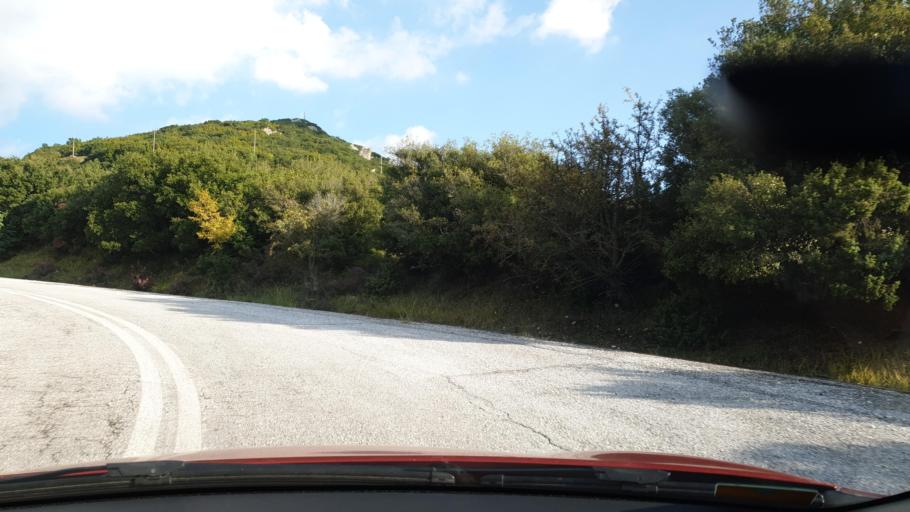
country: GR
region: Central Macedonia
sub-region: Nomos Thessalonikis
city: Peristera
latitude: 40.5225
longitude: 23.2013
